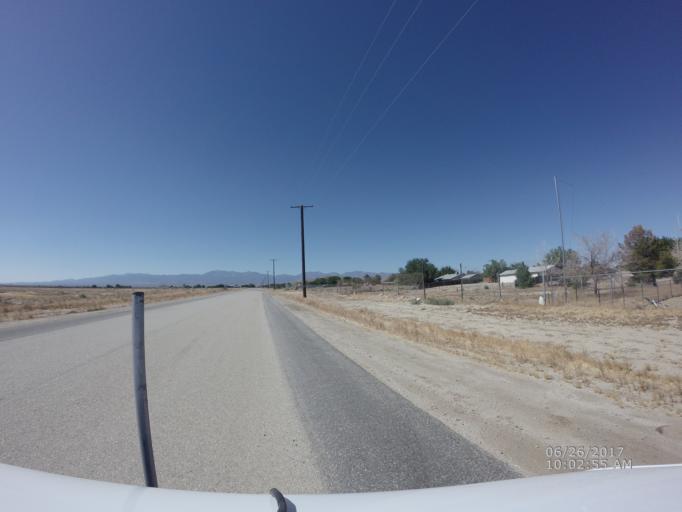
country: US
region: California
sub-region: Los Angeles County
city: Lake Los Angeles
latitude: 34.6252
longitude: -117.8094
